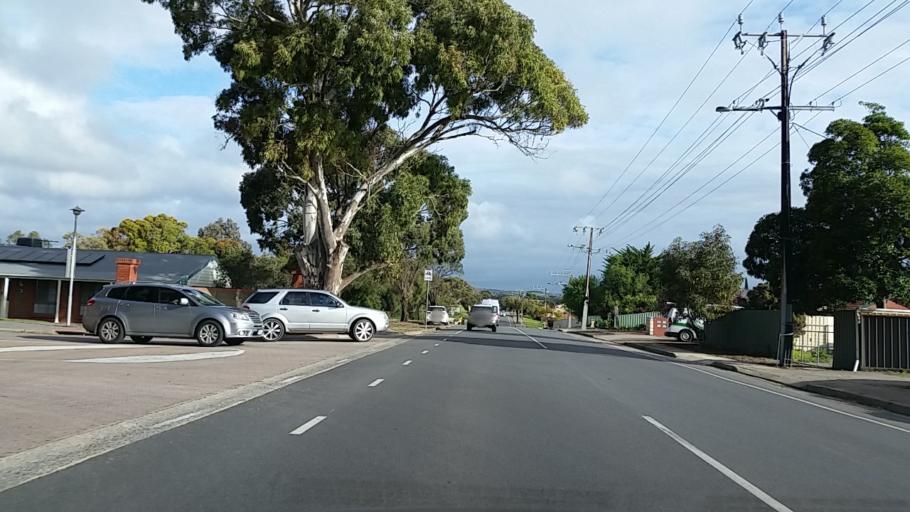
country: AU
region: South Australia
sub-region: Onkaparinga
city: Reynella
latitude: -35.1088
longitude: 138.5351
